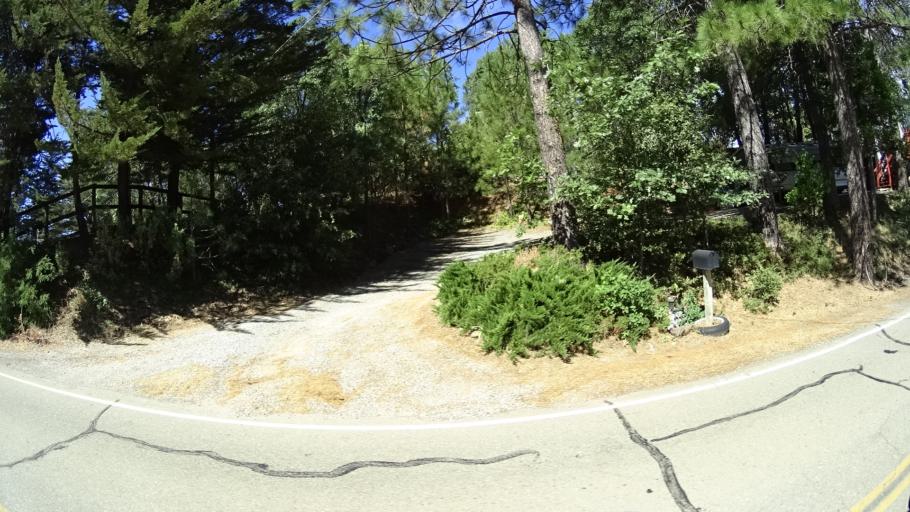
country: US
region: California
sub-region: Amador County
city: Pioneer
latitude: 38.3363
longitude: -120.5414
